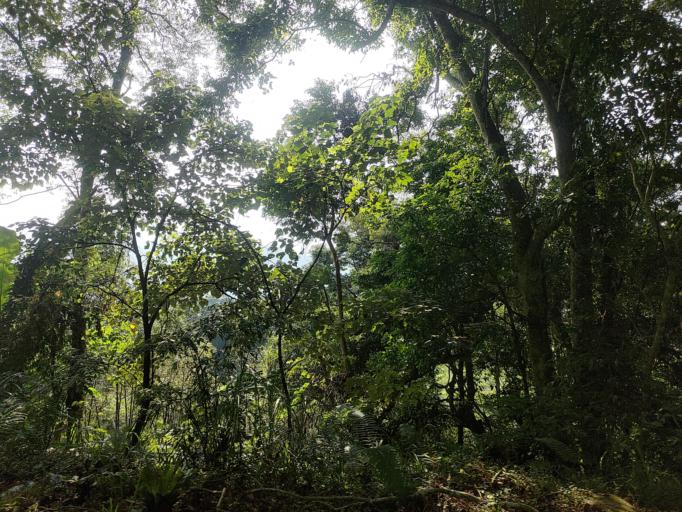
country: TW
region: Taiwan
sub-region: Hsinchu
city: Hsinchu
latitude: 24.6243
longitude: 121.0900
